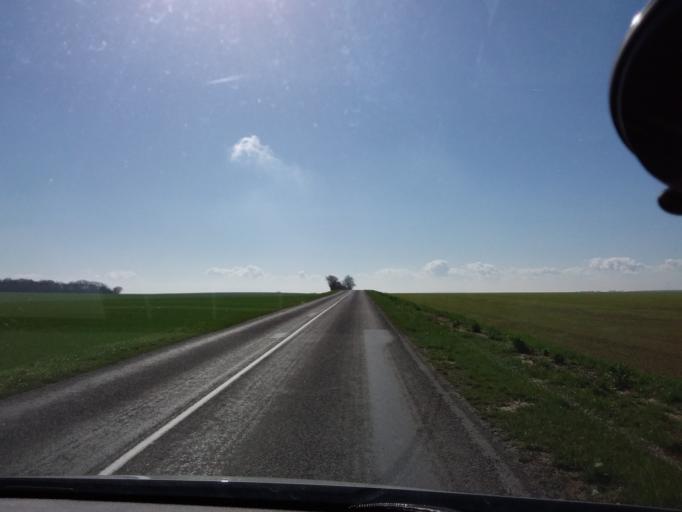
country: FR
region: Picardie
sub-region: Departement de l'Aisne
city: Guignicourt
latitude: 49.4905
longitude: 4.0412
